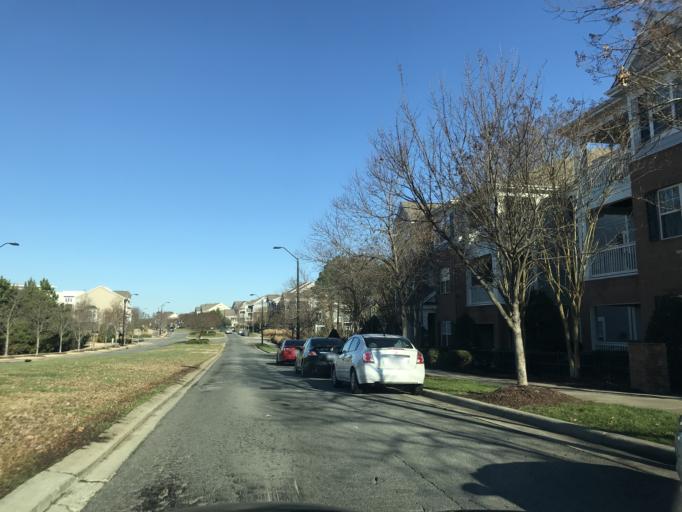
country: US
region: North Carolina
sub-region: Wake County
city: Morrisville
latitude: 35.8974
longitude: -78.8006
